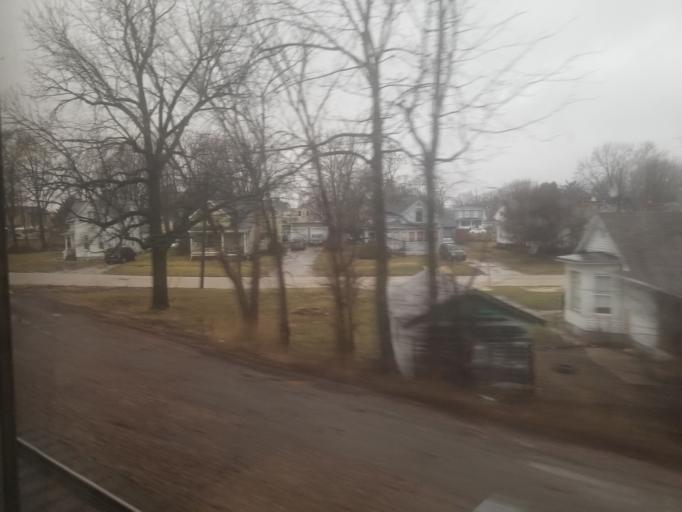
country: US
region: Illinois
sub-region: Knox County
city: Galesburg
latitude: 40.9511
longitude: -90.3576
